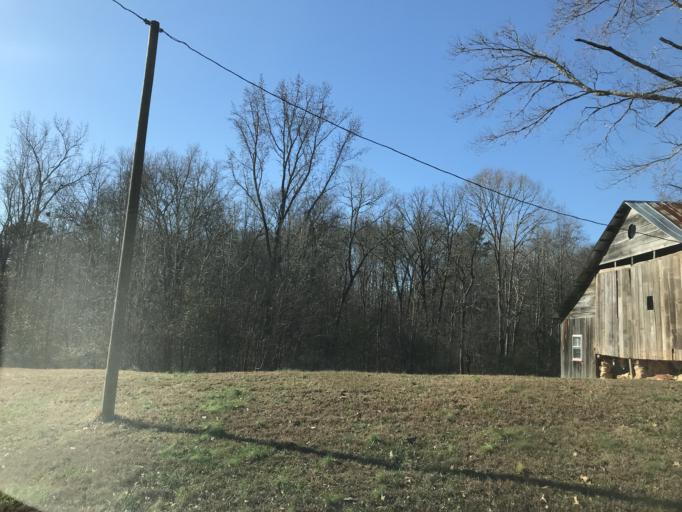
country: US
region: Georgia
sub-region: Paulding County
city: Dallas
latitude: 34.0016
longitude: -84.8980
